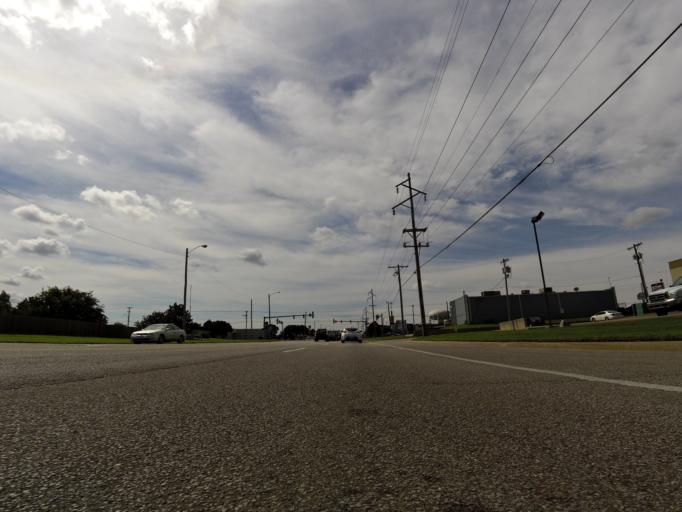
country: US
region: Kansas
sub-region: Sedgwick County
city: Bellaire
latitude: 37.7240
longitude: -97.2624
